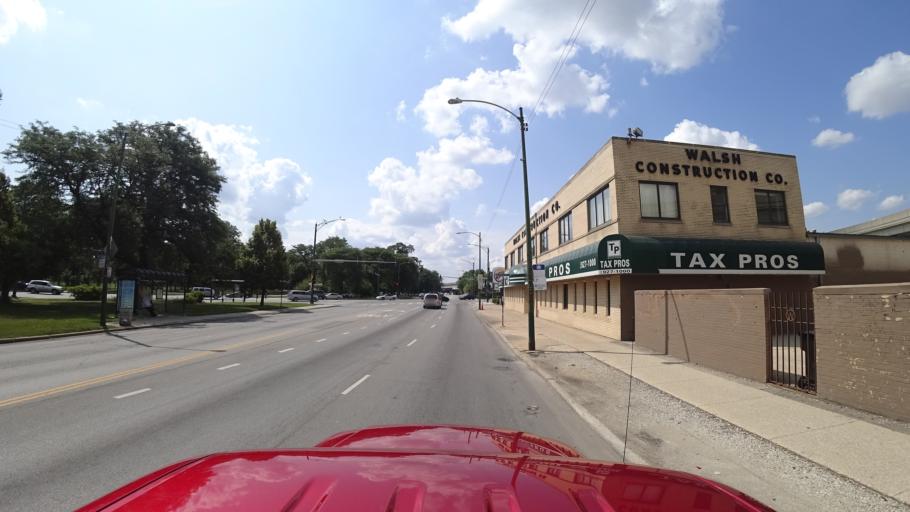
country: US
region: Illinois
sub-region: Cook County
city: Chicago
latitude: 41.8267
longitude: -87.6850
